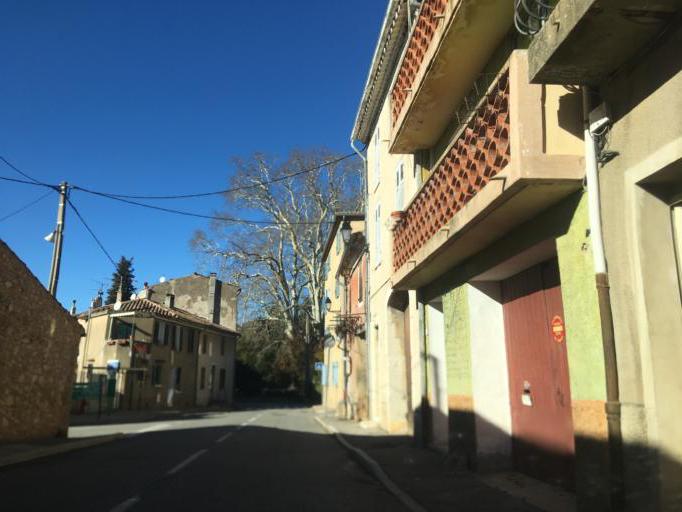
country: FR
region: Provence-Alpes-Cote d'Azur
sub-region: Departement du Var
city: Barjols
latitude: 43.5970
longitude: 5.9620
